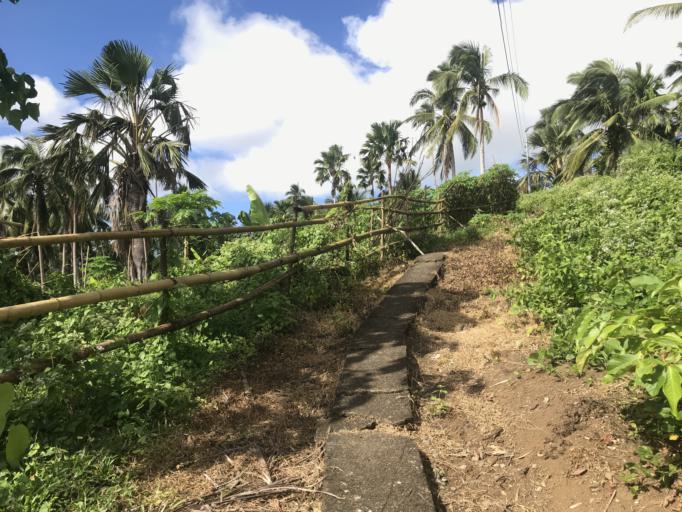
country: PH
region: Calabarzon
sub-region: Province of Quezon
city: Macalelon
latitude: 13.7813
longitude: 122.1426
